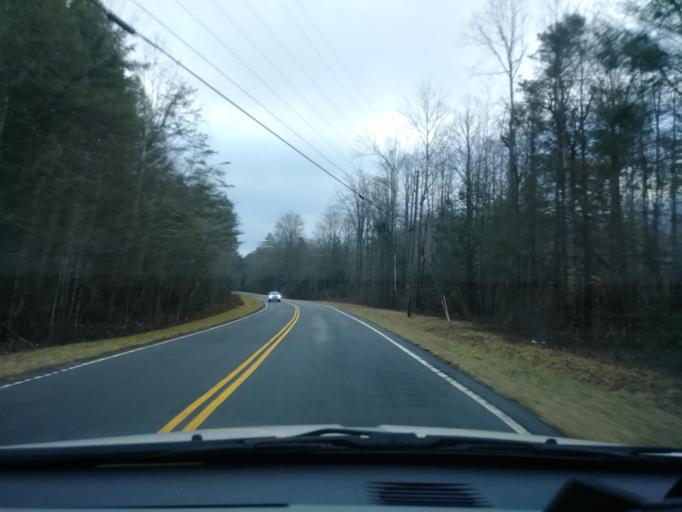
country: US
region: Tennessee
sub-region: Unicoi County
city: Unicoi
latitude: 36.1736
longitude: -82.3079
